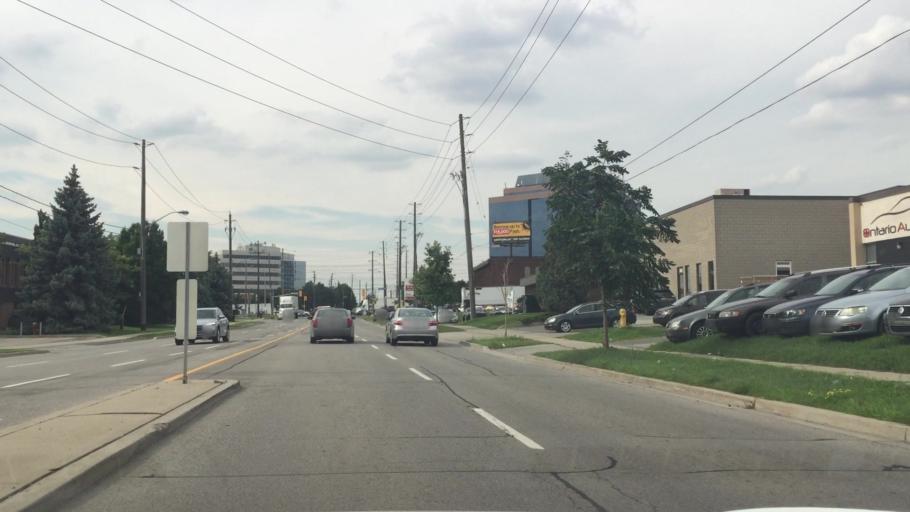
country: CA
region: Ontario
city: Concord
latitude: 43.7688
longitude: -79.5424
